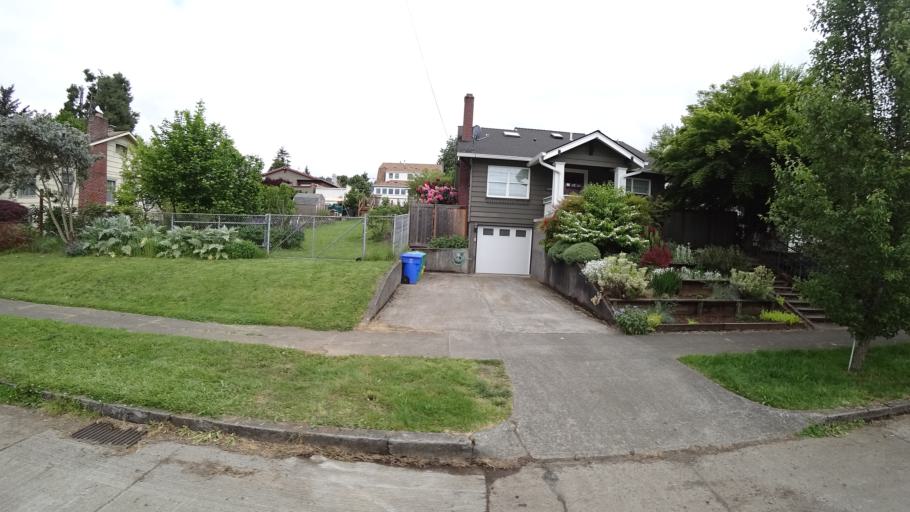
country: US
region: Oregon
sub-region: Multnomah County
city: Lents
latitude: 45.5098
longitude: -122.6066
